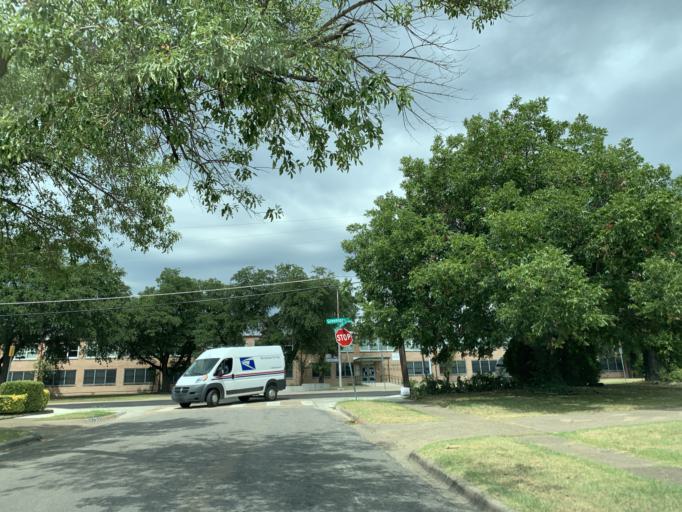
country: US
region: Texas
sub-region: Dallas County
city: Duncanville
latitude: 32.6656
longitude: -96.8288
